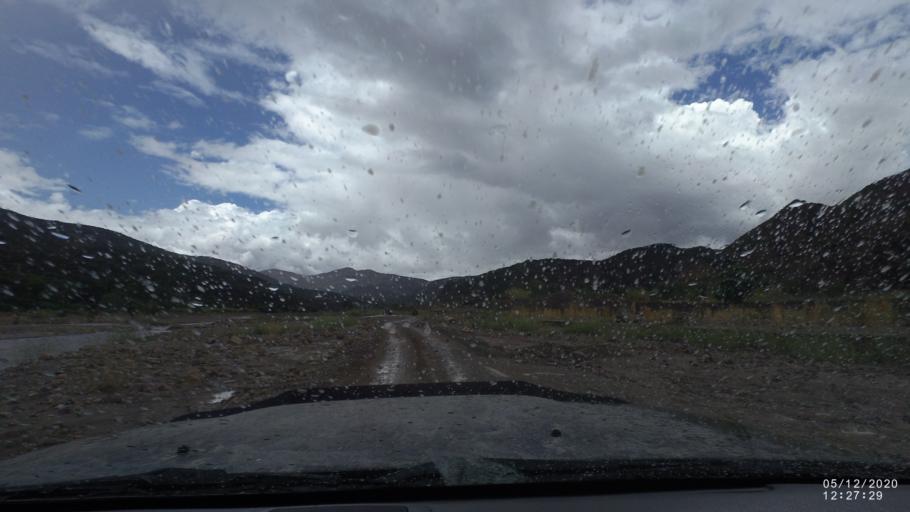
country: BO
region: Cochabamba
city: Sipe Sipe
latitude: -17.5472
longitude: -66.4090
